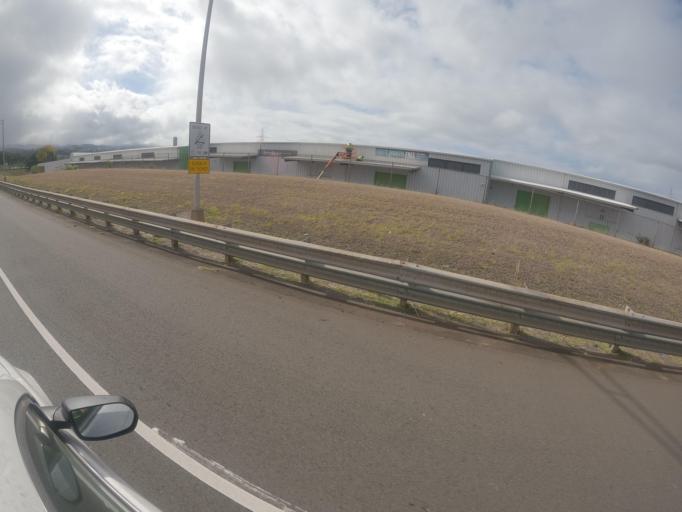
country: US
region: Hawaii
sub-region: Honolulu County
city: Pearl City, Manana
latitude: 21.3928
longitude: -157.9575
